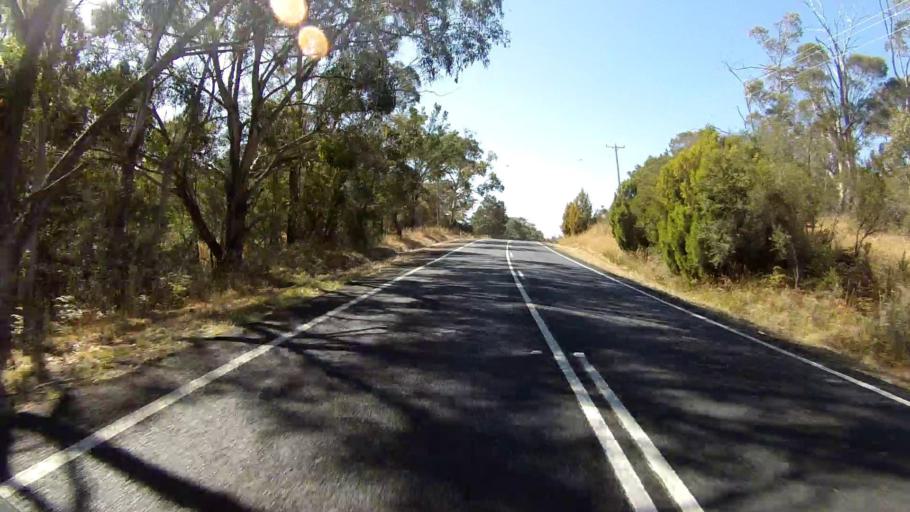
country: AU
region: Tasmania
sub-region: Sorell
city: Sorell
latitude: -42.3893
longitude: 147.9348
